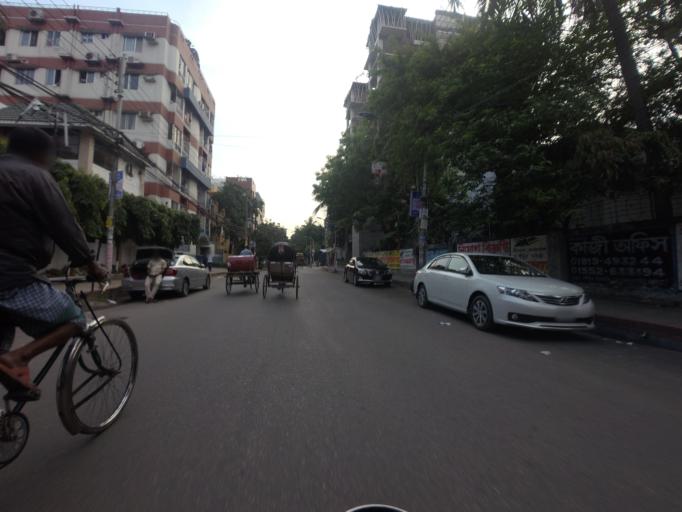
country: BD
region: Dhaka
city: Azimpur
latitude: 23.7384
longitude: 90.3808
